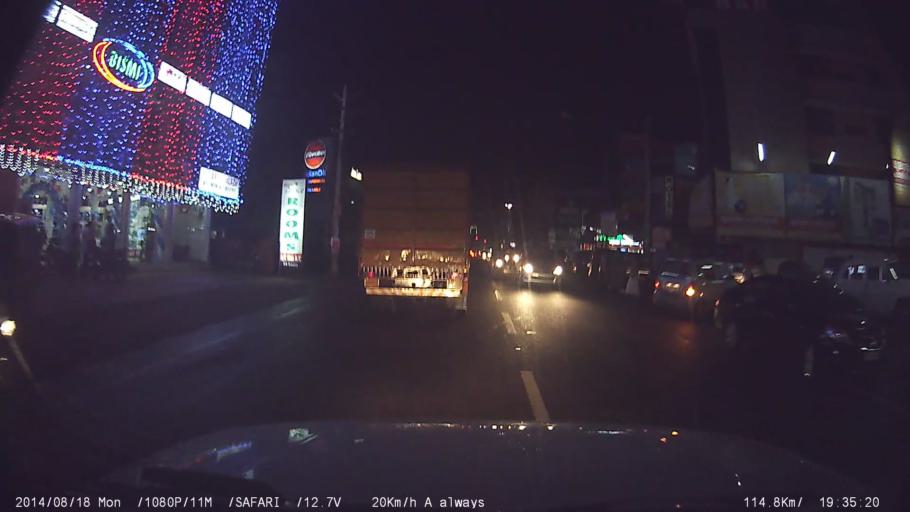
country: IN
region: Kerala
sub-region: Ernakulam
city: Perumpavur
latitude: 10.1129
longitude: 76.4789
